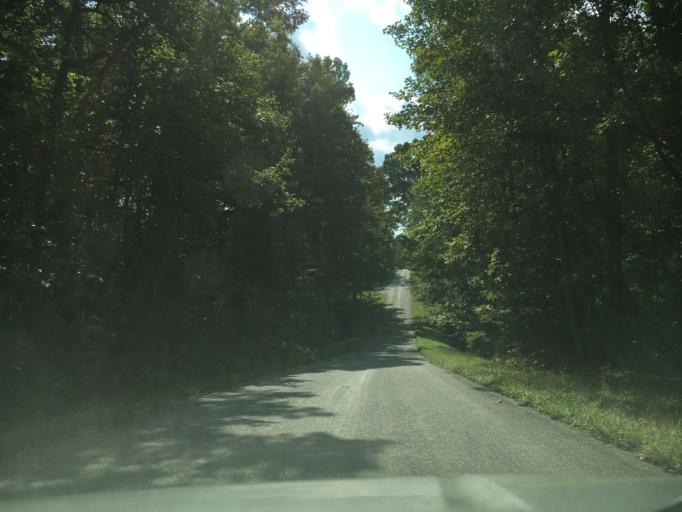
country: US
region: Virginia
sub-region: Campbell County
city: Timberlake
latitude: 37.3290
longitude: -79.1836
